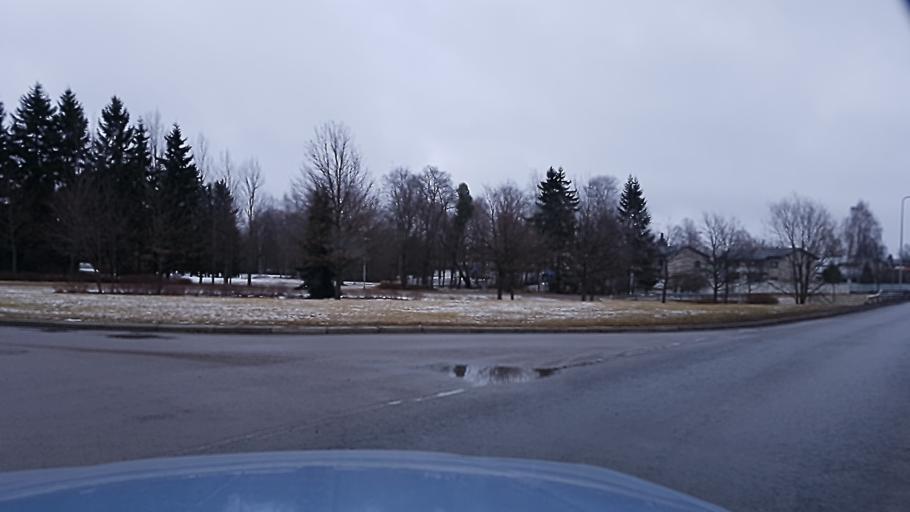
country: FI
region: Uusimaa
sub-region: Helsinki
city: Vantaa
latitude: 60.2921
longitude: 25.0121
